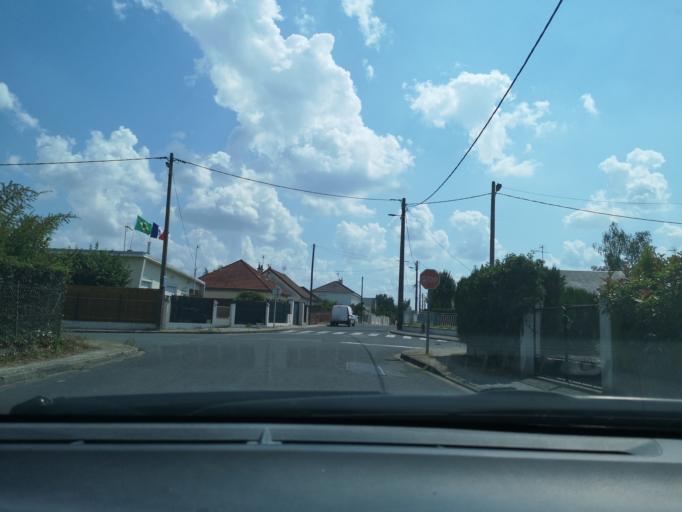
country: FR
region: Centre
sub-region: Departement du Loiret
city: Fleury-les-Aubrais
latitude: 47.9355
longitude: 1.9251
